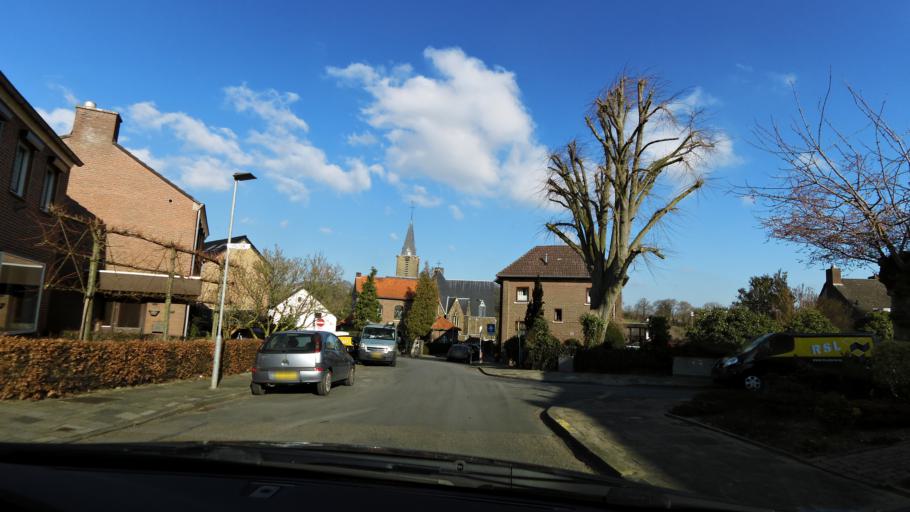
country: NL
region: Limburg
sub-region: Gemeente Nuth
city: Nuth
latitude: 50.9287
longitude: 5.9027
